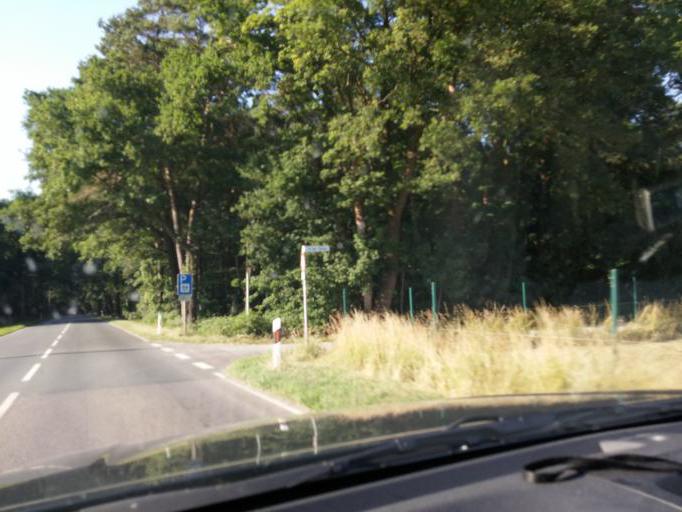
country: DE
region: North Rhine-Westphalia
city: Wegberg
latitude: 51.1838
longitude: 6.3413
